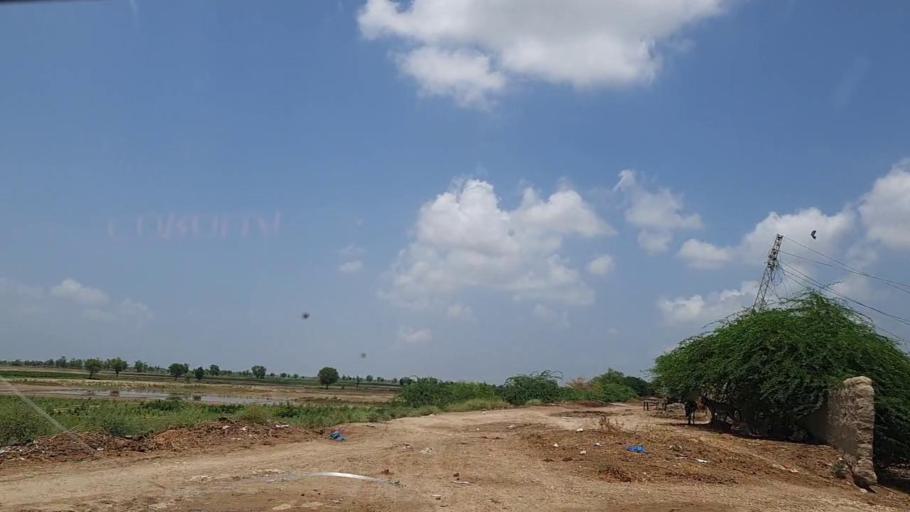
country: PK
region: Sindh
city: Tharu Shah
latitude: 26.9568
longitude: 68.0264
